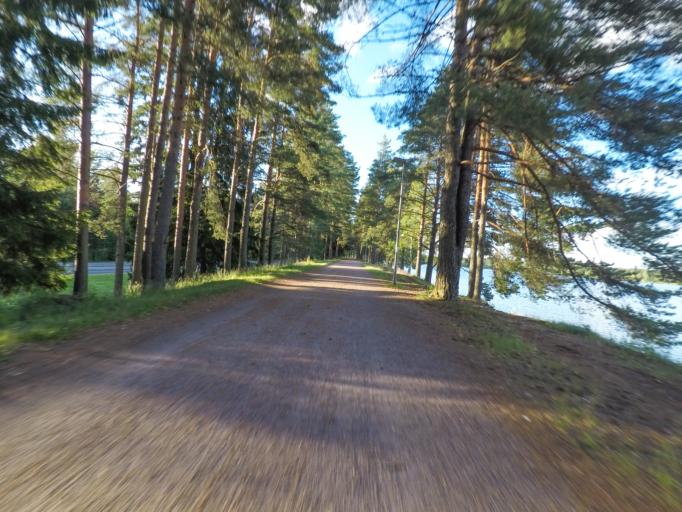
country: FI
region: South Karelia
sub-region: Imatra
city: Imatra
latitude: 61.1769
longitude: 28.7816
